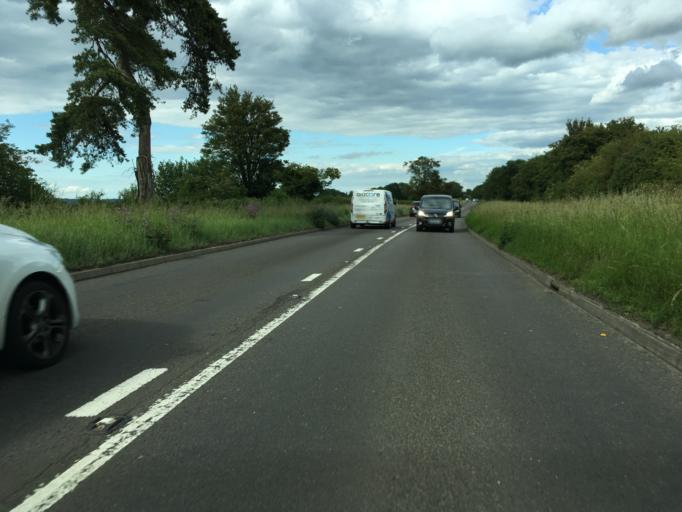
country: GB
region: England
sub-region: Buckinghamshire
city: Stone
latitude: 51.7974
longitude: -0.8903
